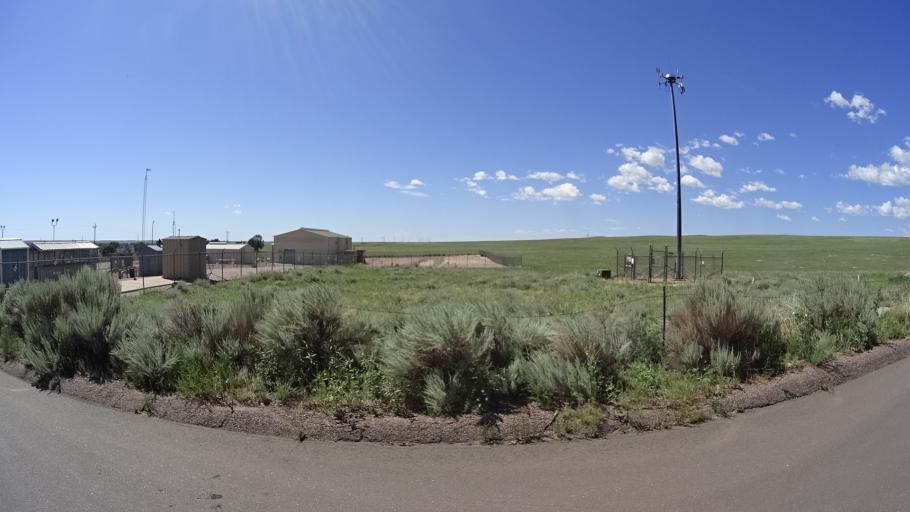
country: US
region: Colorado
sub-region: El Paso County
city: Security-Widefield
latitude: 38.7809
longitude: -104.6750
